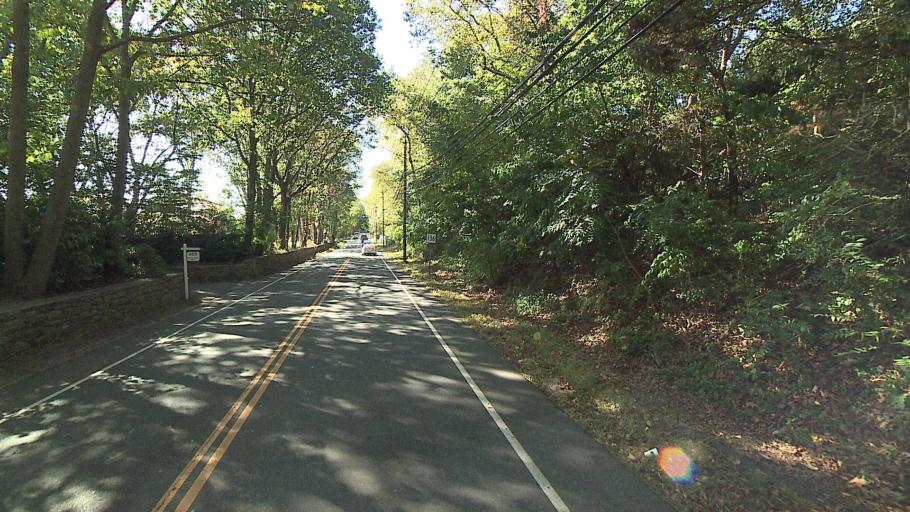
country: US
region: Connecticut
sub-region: Fairfield County
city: East Norwalk
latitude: 41.1130
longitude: -73.3775
